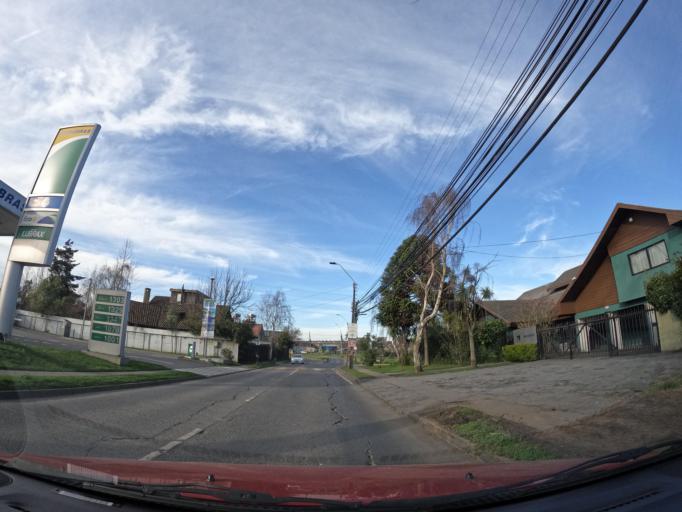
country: CL
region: Biobio
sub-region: Provincia de Concepcion
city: Concepcion
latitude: -36.7888
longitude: -73.0560
